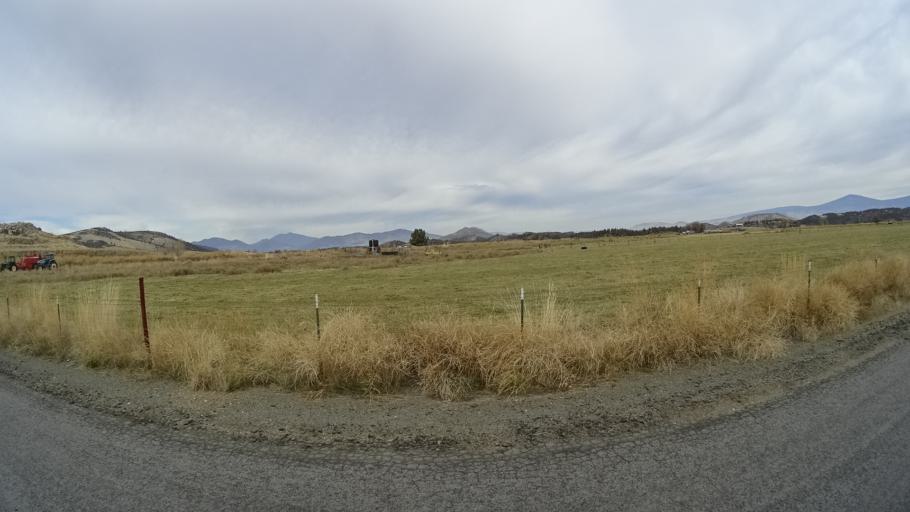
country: US
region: California
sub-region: Siskiyou County
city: Montague
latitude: 41.6581
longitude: -122.5152
